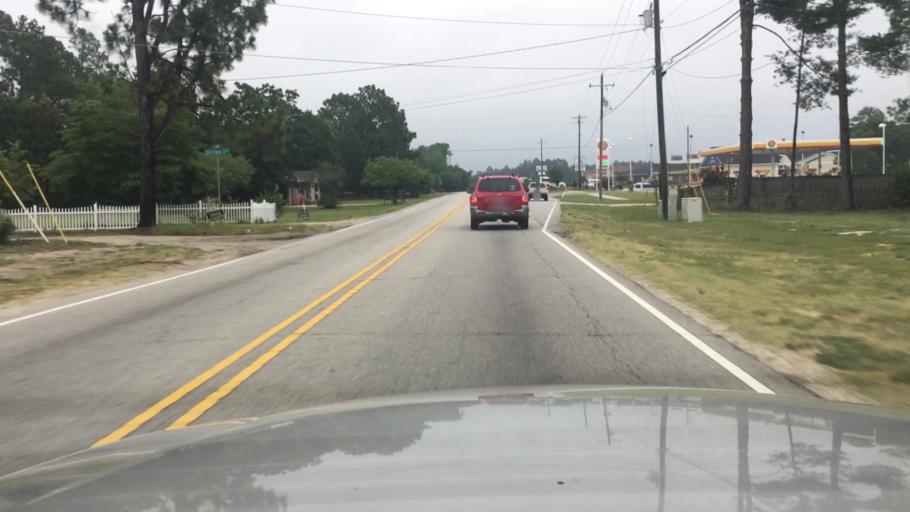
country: US
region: North Carolina
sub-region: Cumberland County
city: Hope Mills
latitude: 34.9792
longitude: -78.9805
